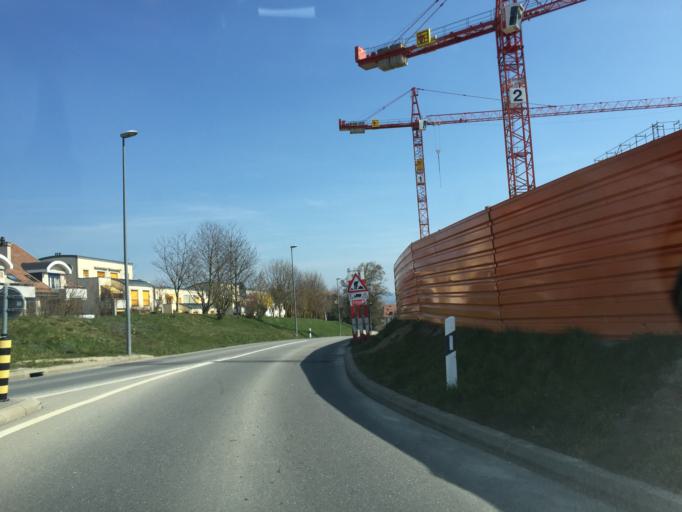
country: CH
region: Vaud
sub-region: Morges District
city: Cossonay
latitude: 46.6147
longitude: 6.5021
